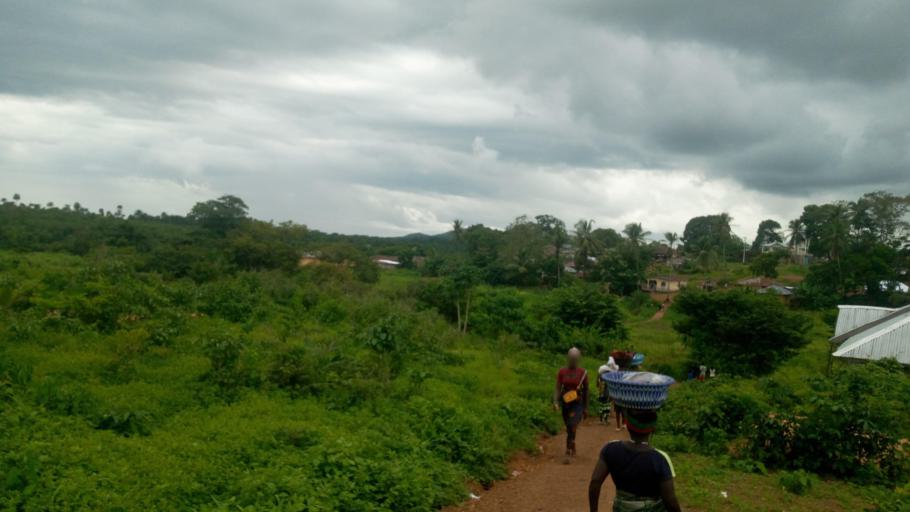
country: SL
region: Southern Province
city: Mogbwemo
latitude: 7.6024
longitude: -12.1787
